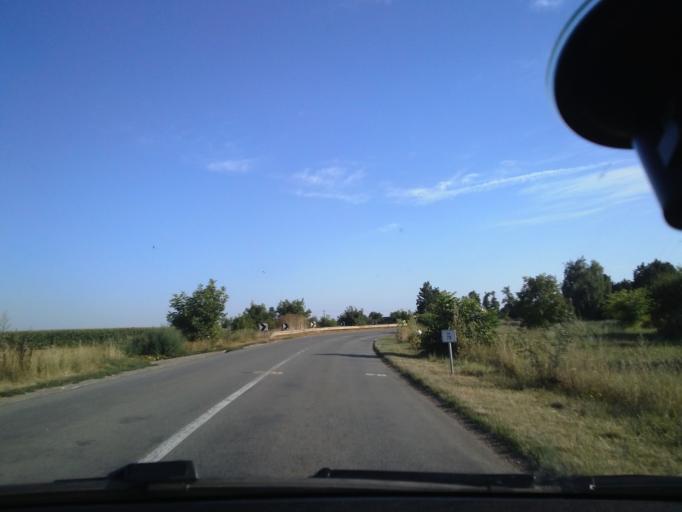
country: RS
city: Doroslovo
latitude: 45.6168
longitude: 19.1969
